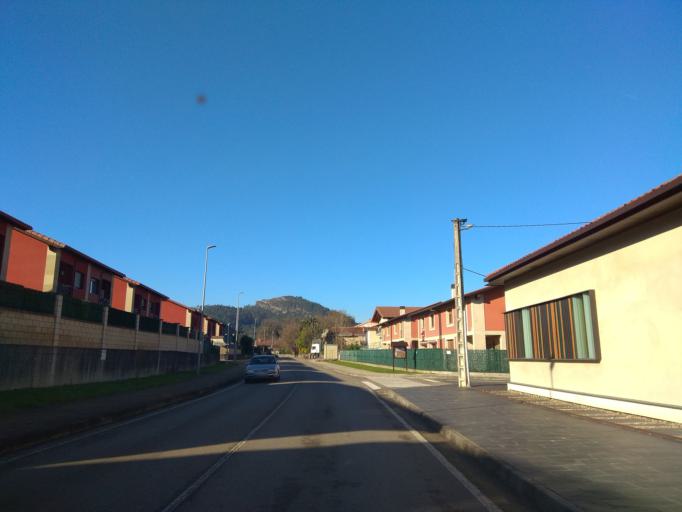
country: ES
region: Cantabria
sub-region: Provincia de Cantabria
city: Entrambasaguas
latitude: 43.3759
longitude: -3.6780
